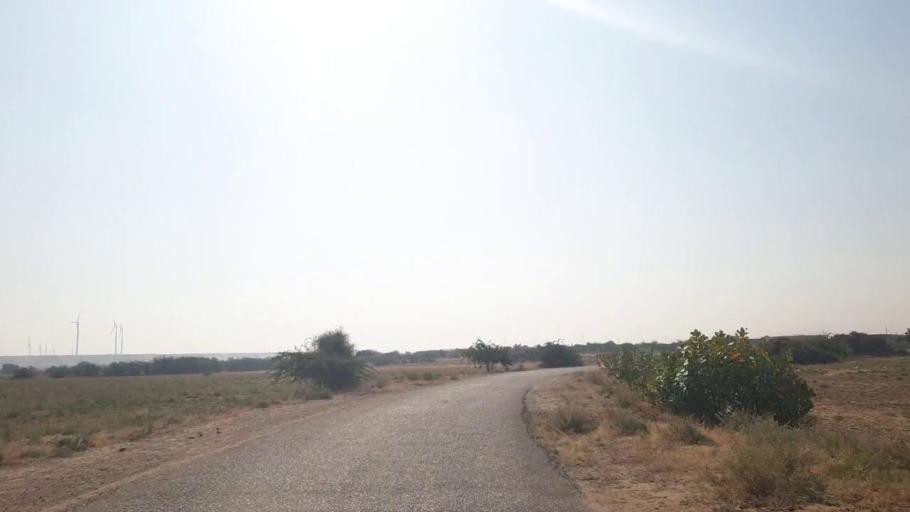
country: PK
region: Sindh
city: Thatta
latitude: 25.1305
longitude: 67.7759
